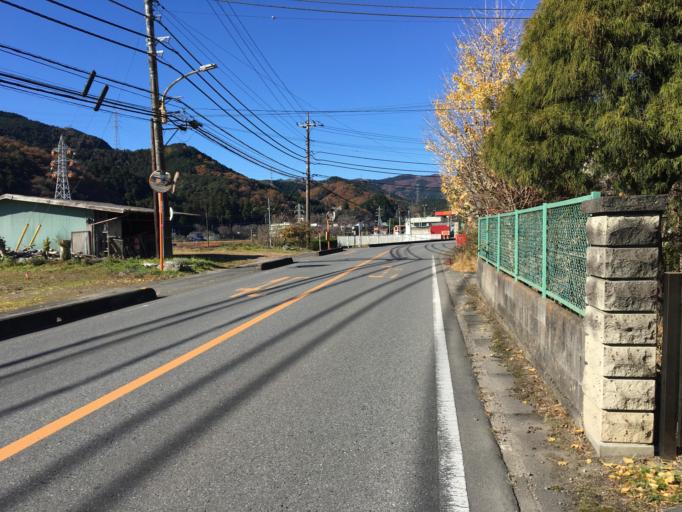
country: JP
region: Saitama
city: Ogawa
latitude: 36.0501
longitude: 139.2114
